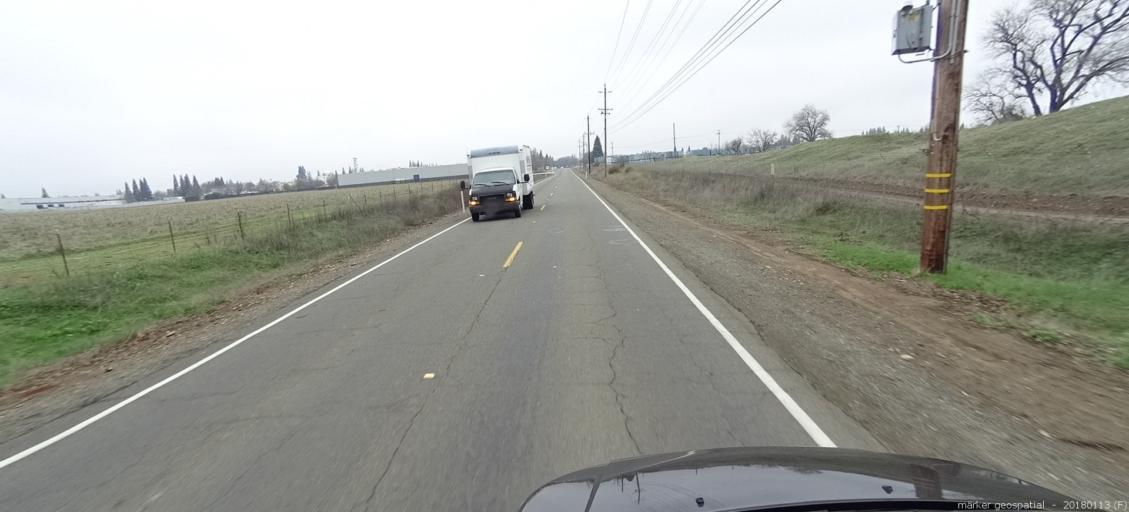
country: US
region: California
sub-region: Sacramento County
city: Gold River
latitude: 38.5912
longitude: -121.2526
